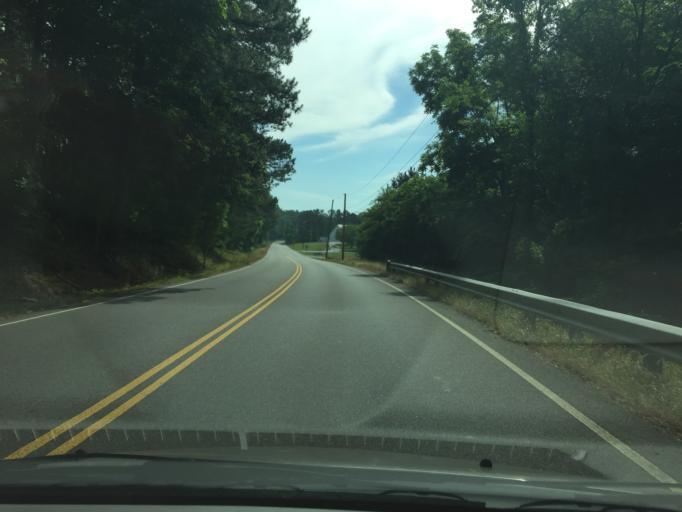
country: US
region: Tennessee
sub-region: Hamilton County
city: Collegedale
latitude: 35.1131
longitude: -84.9803
